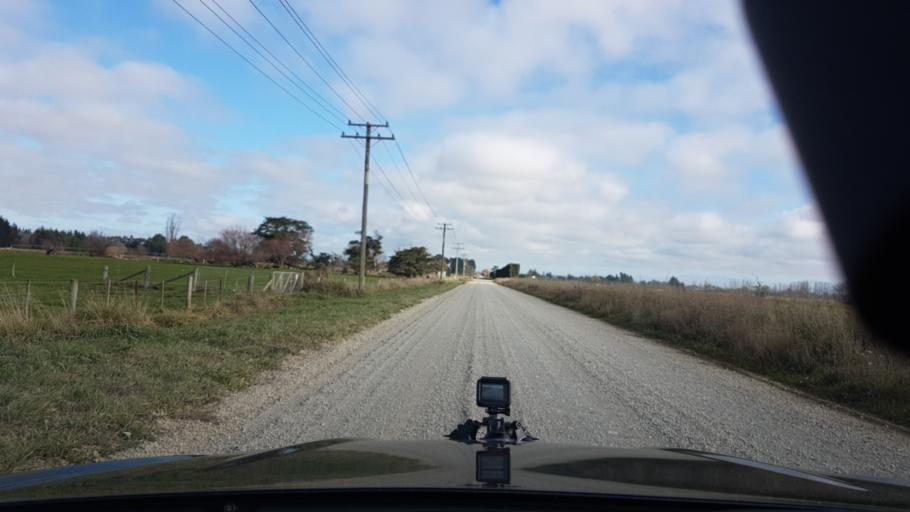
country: NZ
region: Canterbury
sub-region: Waimakariri District
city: Woodend
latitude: -43.3220
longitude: 172.6265
